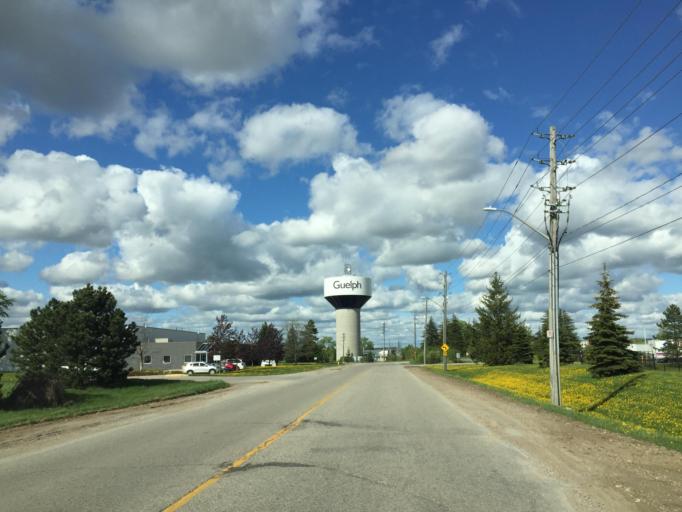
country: CA
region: Ontario
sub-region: Wellington County
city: Guelph
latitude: 43.4905
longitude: -80.2021
